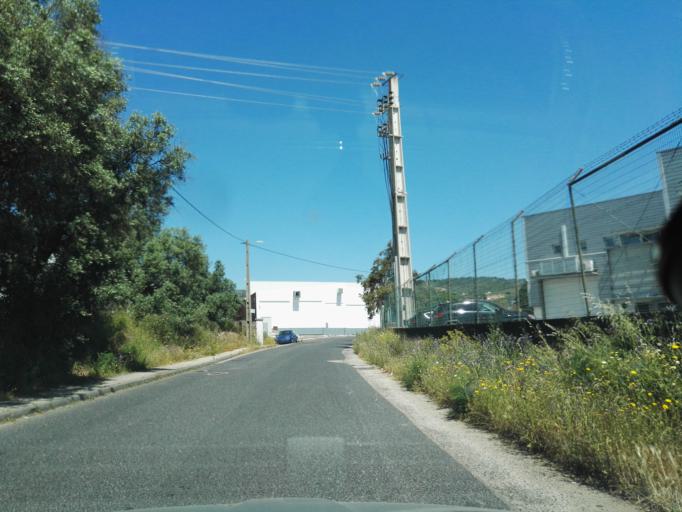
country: PT
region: Lisbon
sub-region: Vila Franca de Xira
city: Sobralinho
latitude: 38.9060
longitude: -9.0269
